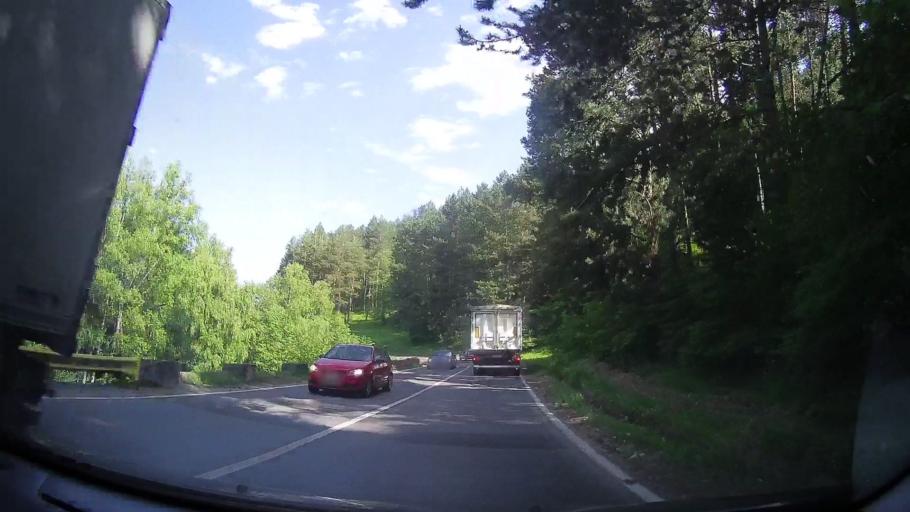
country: RO
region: Prahova
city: Maneciu
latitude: 45.3301
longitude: 25.9748
